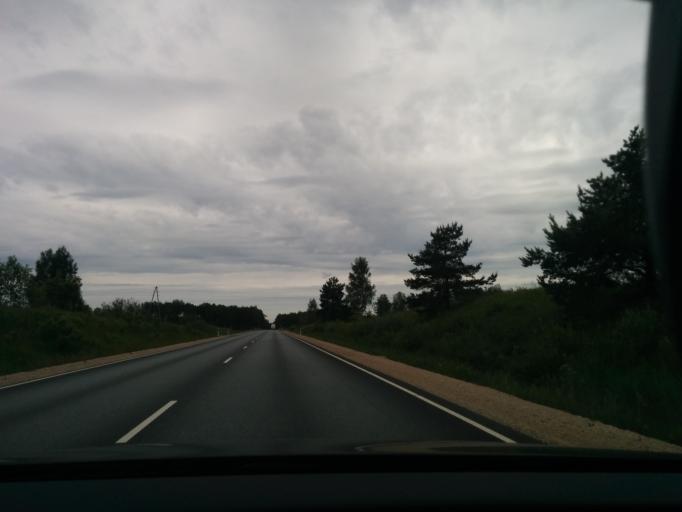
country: LV
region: Ikskile
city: Ikskile
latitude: 56.8831
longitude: 24.5032
